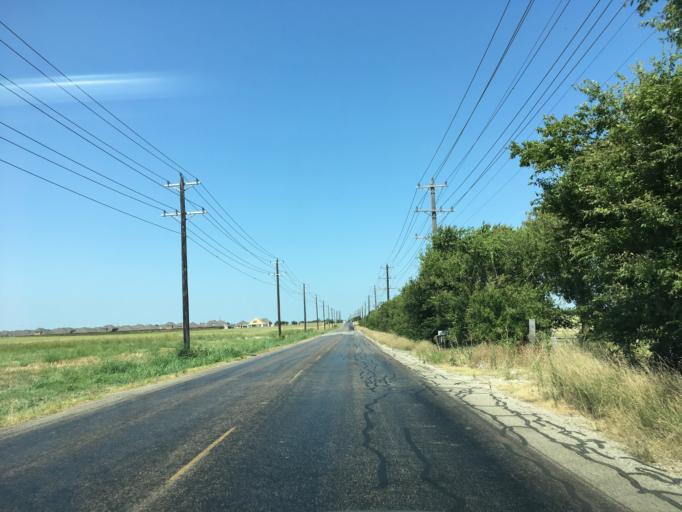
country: US
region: Texas
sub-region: Collin County
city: Prosper
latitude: 33.2038
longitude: -96.7750
